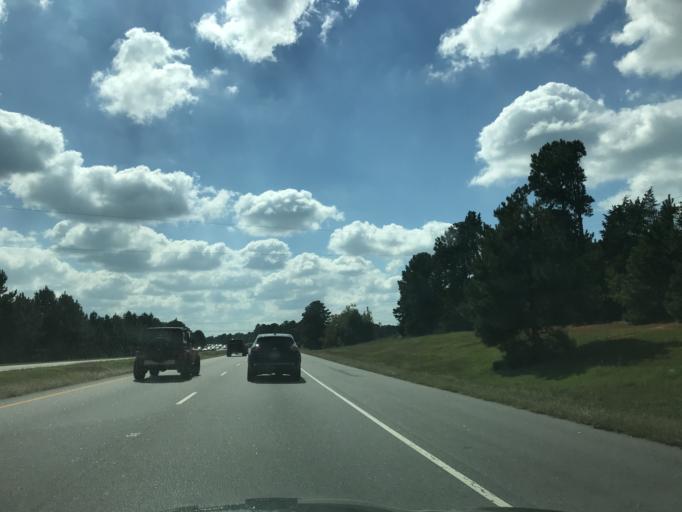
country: US
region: North Carolina
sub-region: Wake County
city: Wake Forest
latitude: 35.9407
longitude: -78.5407
